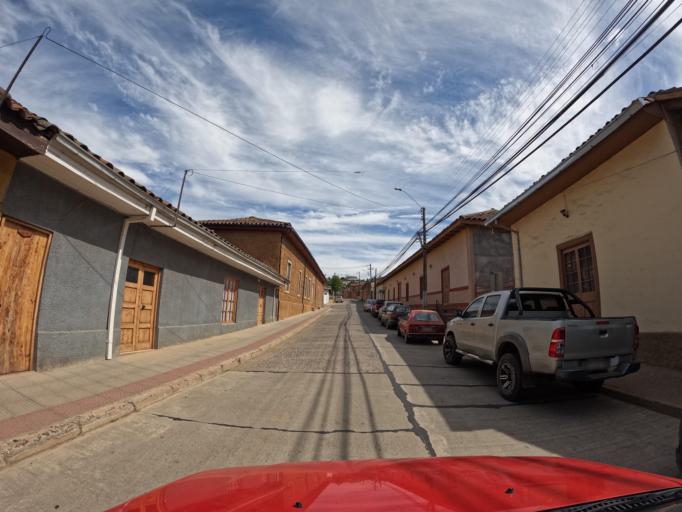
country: CL
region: Maule
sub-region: Provincia de Talca
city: Constitucion
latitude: -35.0954
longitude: -72.0193
